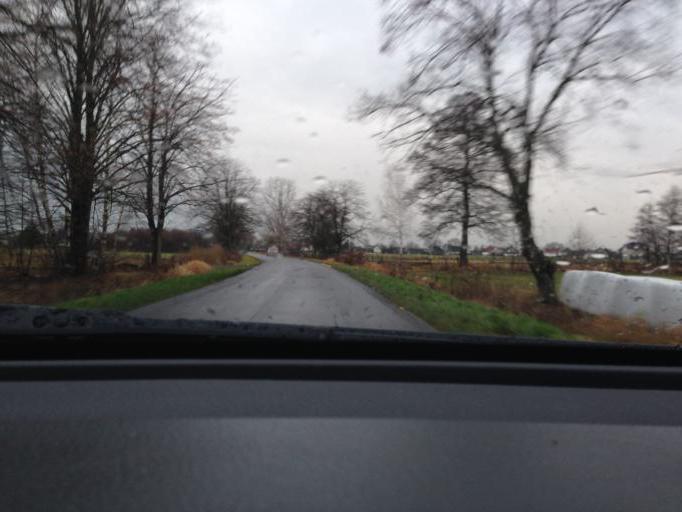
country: PL
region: Opole Voivodeship
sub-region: Powiat opolski
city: Wegry
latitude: 50.7305
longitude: 18.0566
